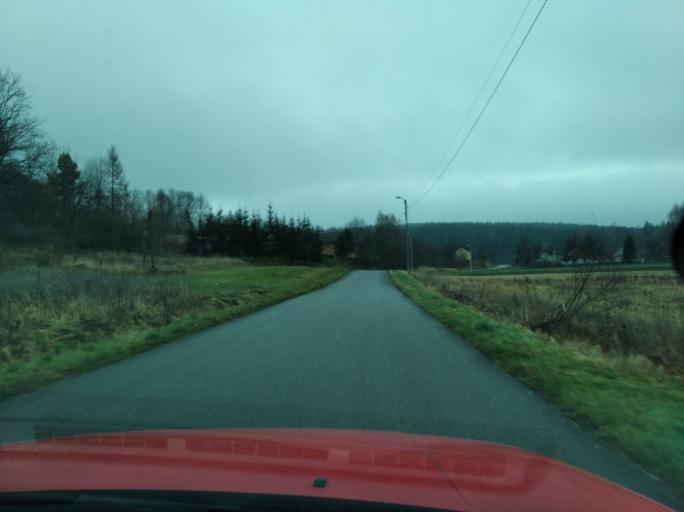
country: PL
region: Subcarpathian Voivodeship
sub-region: Powiat przemyski
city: Nienadowa
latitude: 49.8544
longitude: 22.4231
